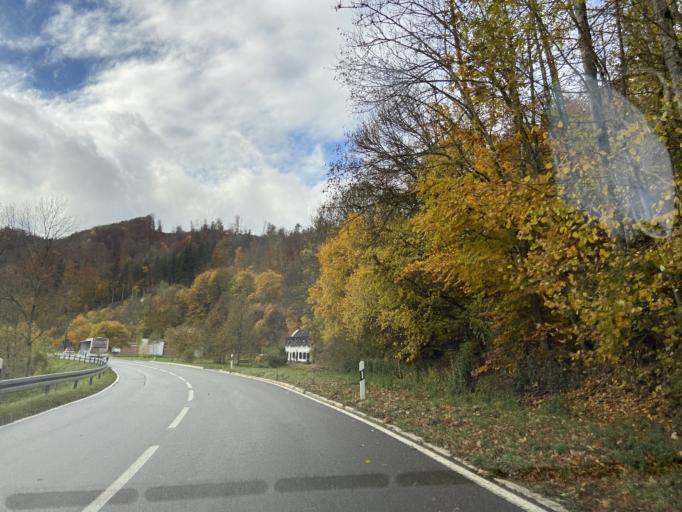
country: DE
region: Baden-Wuerttemberg
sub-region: Tuebingen Region
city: Beuron
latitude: 48.0557
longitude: 8.9699
